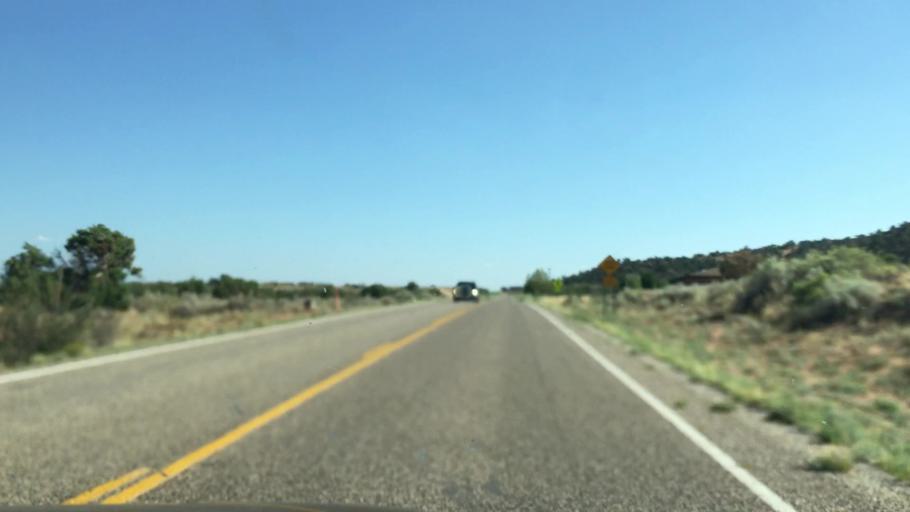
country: US
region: Arizona
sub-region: Coconino County
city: Fredonia
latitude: 36.8824
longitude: -112.7391
